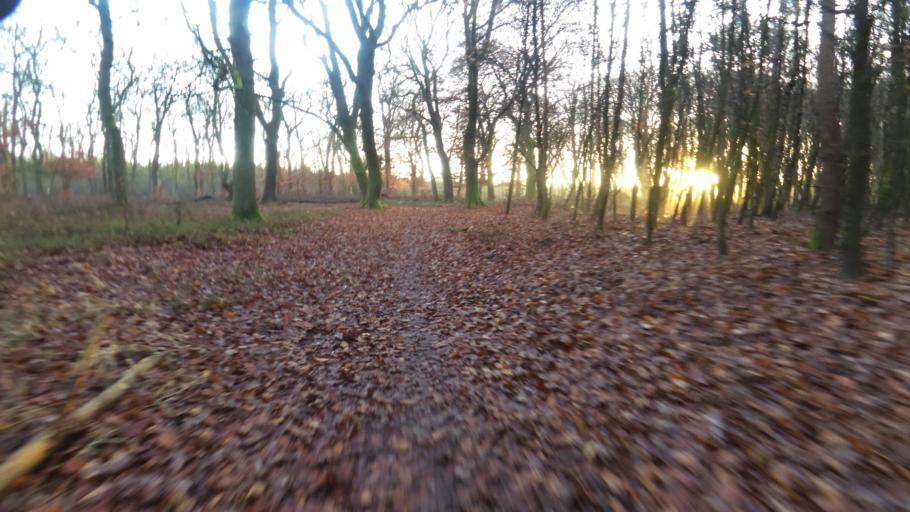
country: NL
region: Gelderland
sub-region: Gemeente Apeldoorn
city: Uddel
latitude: 52.2305
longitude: 5.8228
